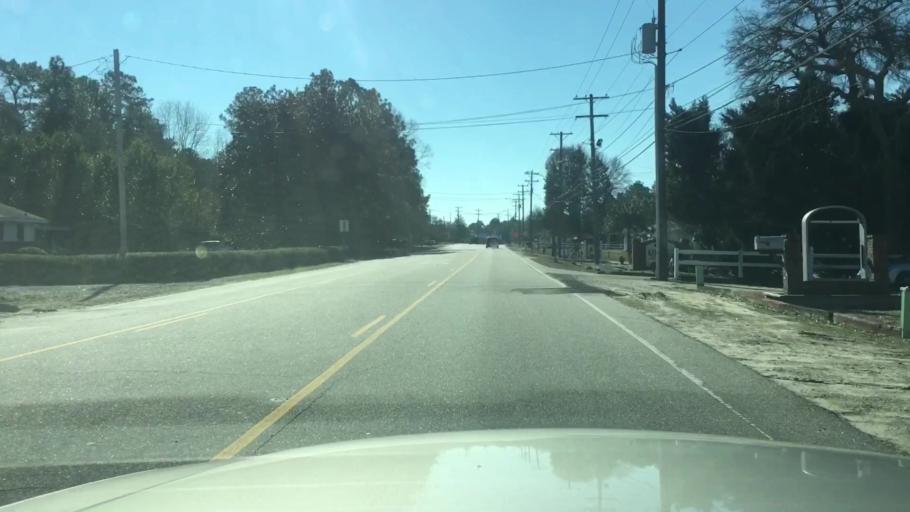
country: US
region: North Carolina
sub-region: Cumberland County
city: Hope Mills
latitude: 35.0185
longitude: -78.9353
